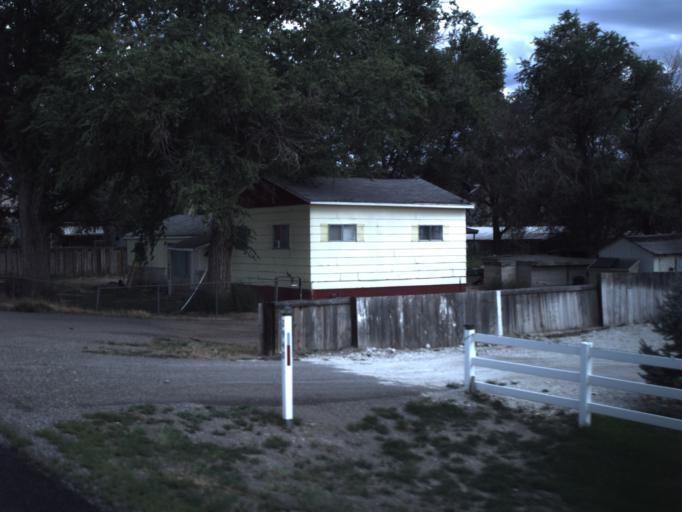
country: US
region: Utah
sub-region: Sevier County
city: Richfield
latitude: 38.7738
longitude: -112.0323
